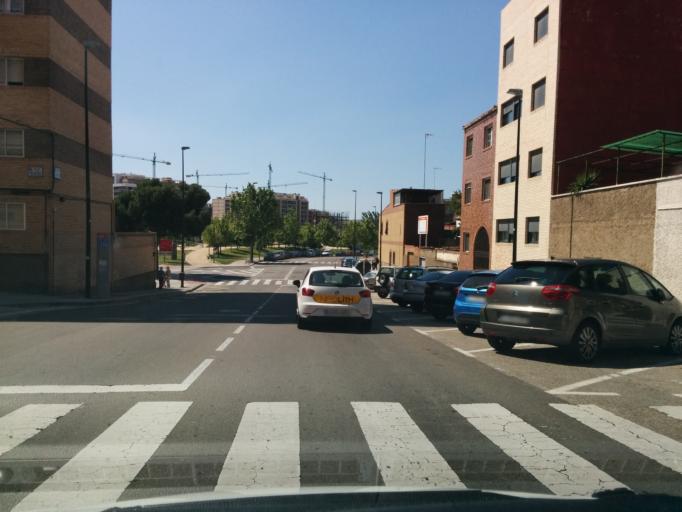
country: ES
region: Aragon
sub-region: Provincia de Zaragoza
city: Zaragoza
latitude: 41.6233
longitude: -0.8761
